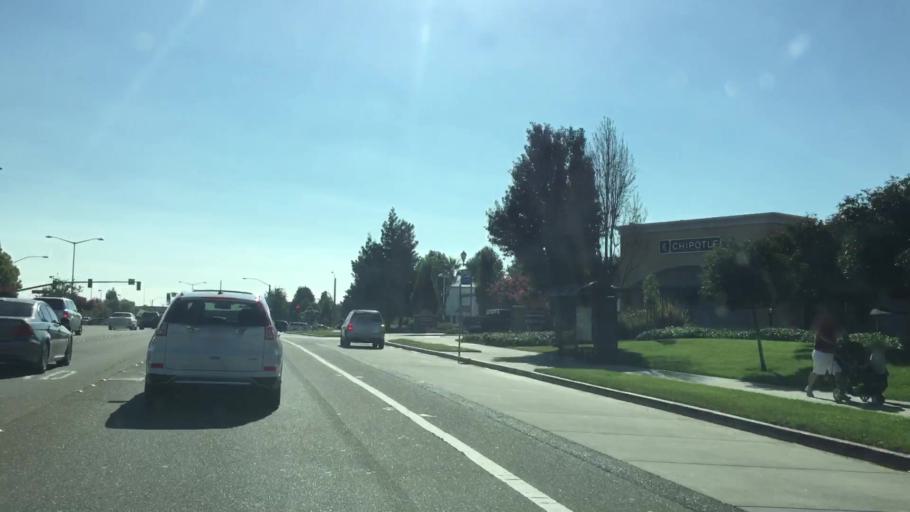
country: US
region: California
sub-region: Contra Costa County
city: Oakley
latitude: 37.9616
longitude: -121.7493
